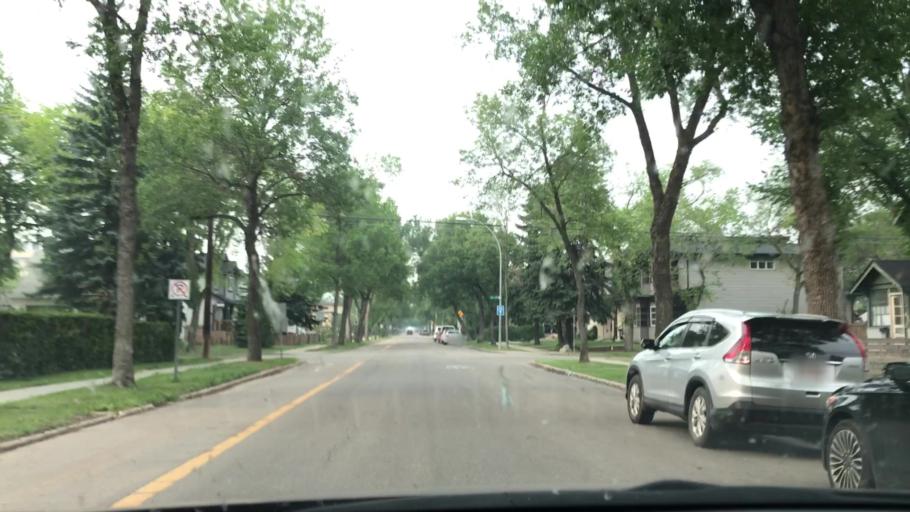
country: CA
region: Alberta
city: Edmonton
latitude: 53.5616
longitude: -113.5412
